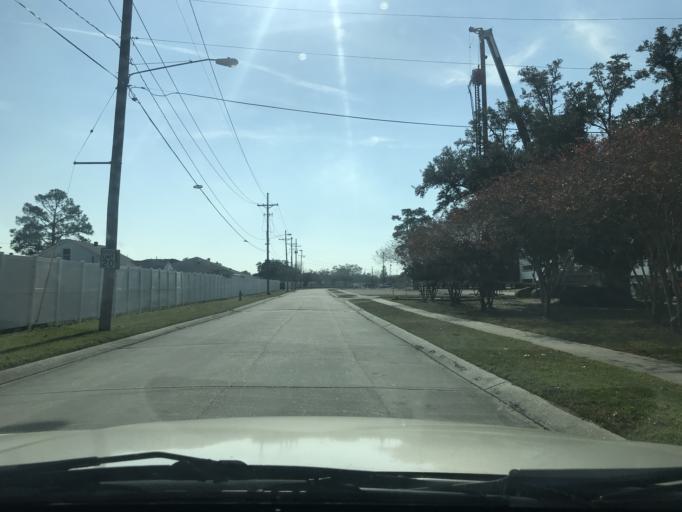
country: US
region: Louisiana
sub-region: Jefferson Parish
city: Marrero
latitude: 29.8918
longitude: -90.0931
